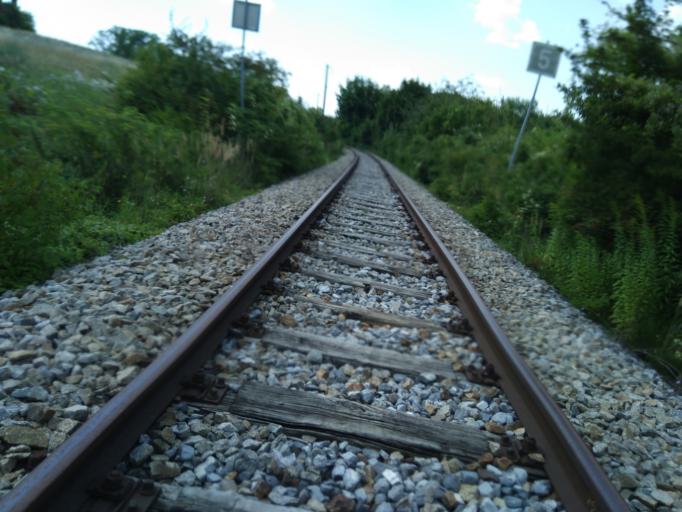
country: AT
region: Lower Austria
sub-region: Politischer Bezirk Ganserndorf
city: Bad Pirawarth
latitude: 48.4597
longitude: 16.6160
